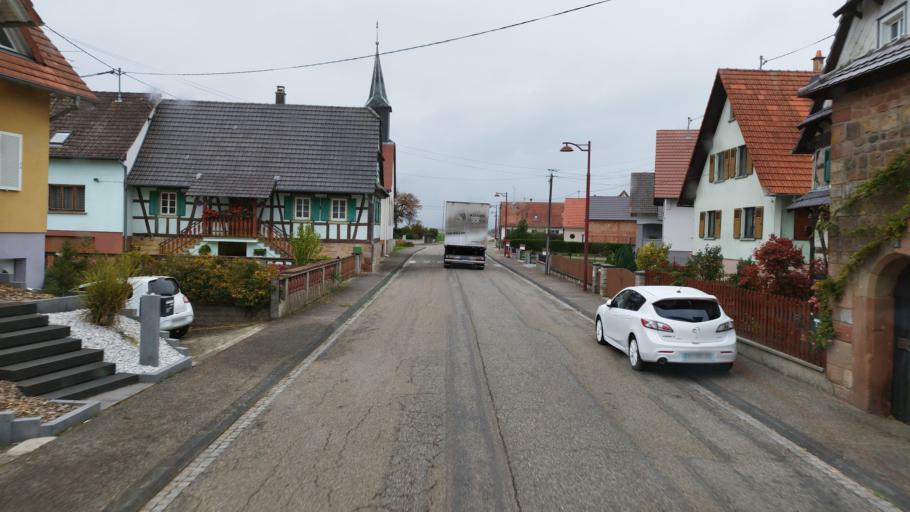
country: DE
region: Rheinland-Pfalz
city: Kapsweyer
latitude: 48.9939
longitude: 8.0202
